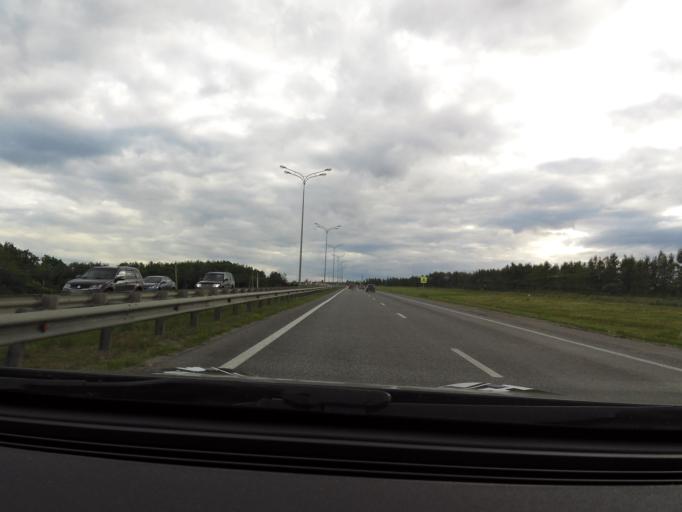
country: RU
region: Tatarstan
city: Osinovo
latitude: 55.7640
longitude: 48.8218
